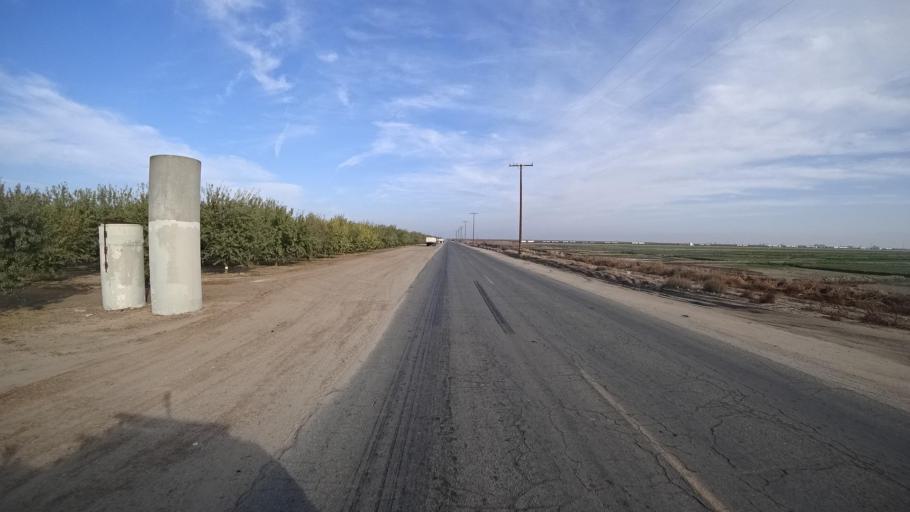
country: US
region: California
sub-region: Kern County
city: Delano
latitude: 35.7797
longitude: -119.2053
